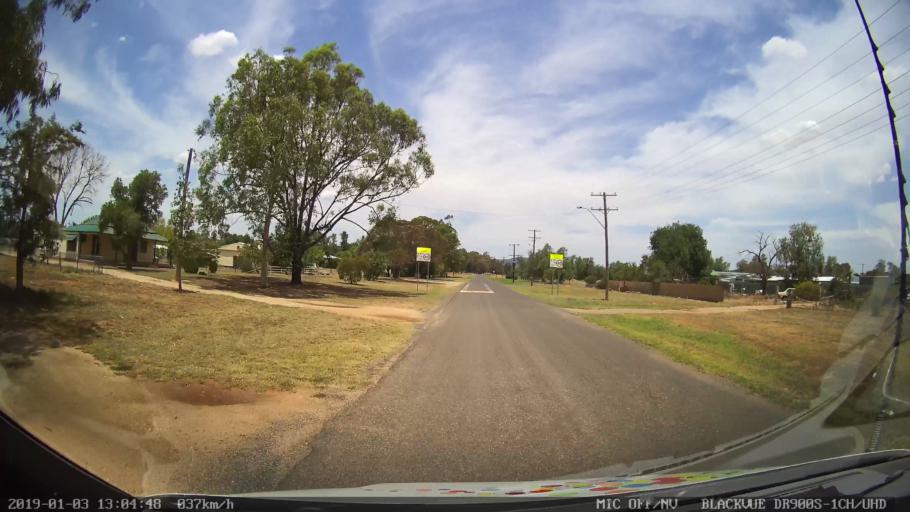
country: AU
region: New South Wales
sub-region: Cabonne
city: Canowindra
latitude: -33.6158
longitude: 148.4398
